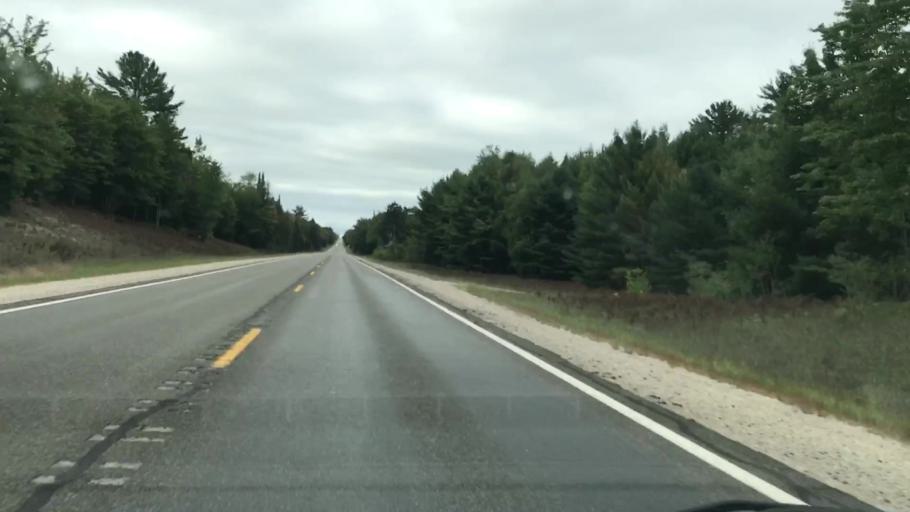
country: US
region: Michigan
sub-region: Luce County
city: Newberry
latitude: 46.2383
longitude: -85.5722
